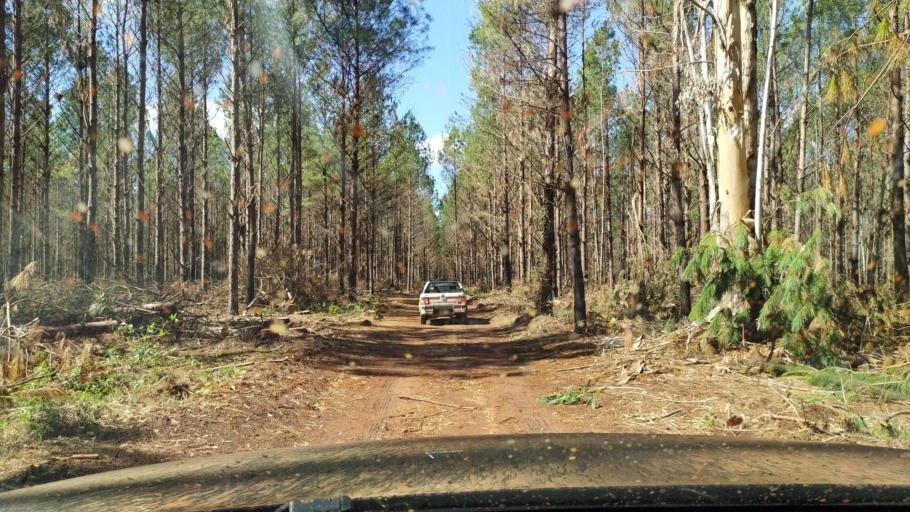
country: AR
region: Corrientes
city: Santo Tome
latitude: -28.4102
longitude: -56.0126
